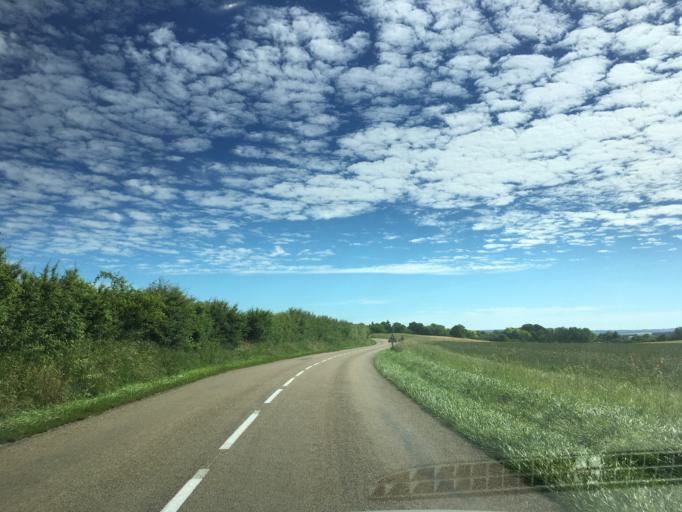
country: FR
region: Bourgogne
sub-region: Departement de l'Yonne
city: Saint-Georges-sur-Baulche
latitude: 47.7766
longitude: 3.5402
